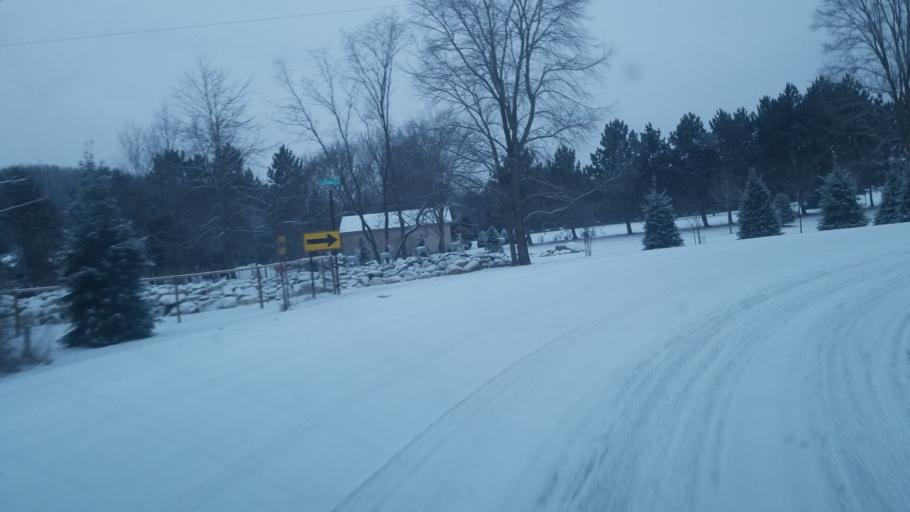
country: US
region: Michigan
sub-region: Osceola County
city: Reed City
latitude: 43.8219
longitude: -85.4238
